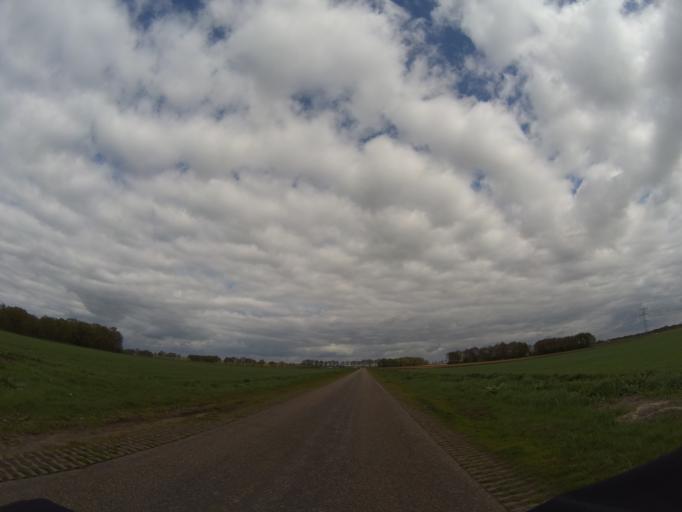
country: NL
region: Drenthe
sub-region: Gemeente Coevorden
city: Sleen
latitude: 52.7784
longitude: 6.8388
